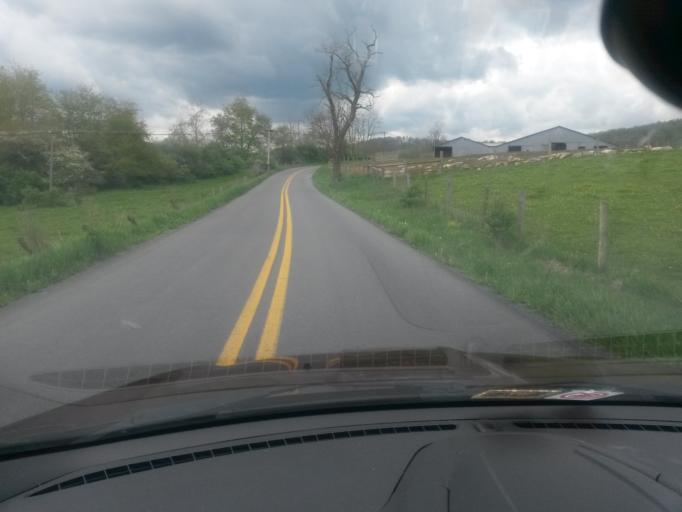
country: US
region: West Virginia
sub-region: Greenbrier County
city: Lewisburg
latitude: 37.9311
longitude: -80.3951
